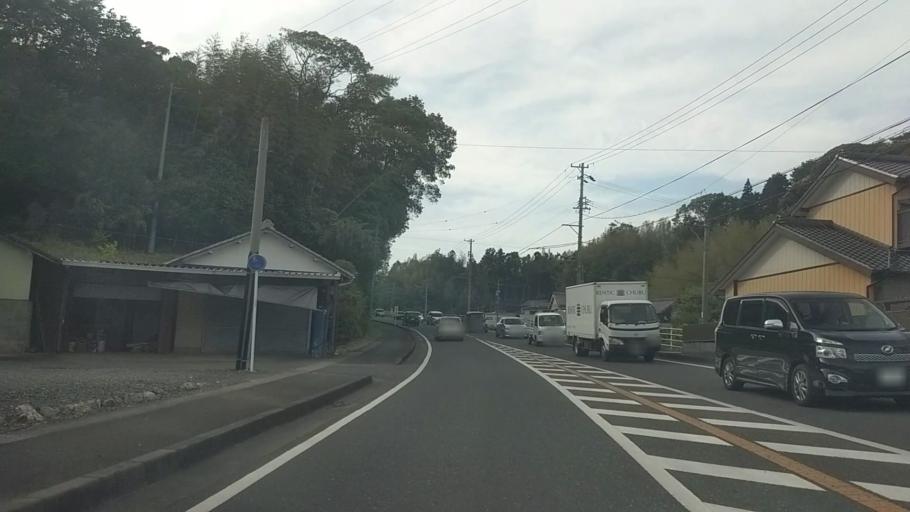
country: JP
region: Shizuoka
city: Hamamatsu
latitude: 34.7627
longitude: 137.6482
